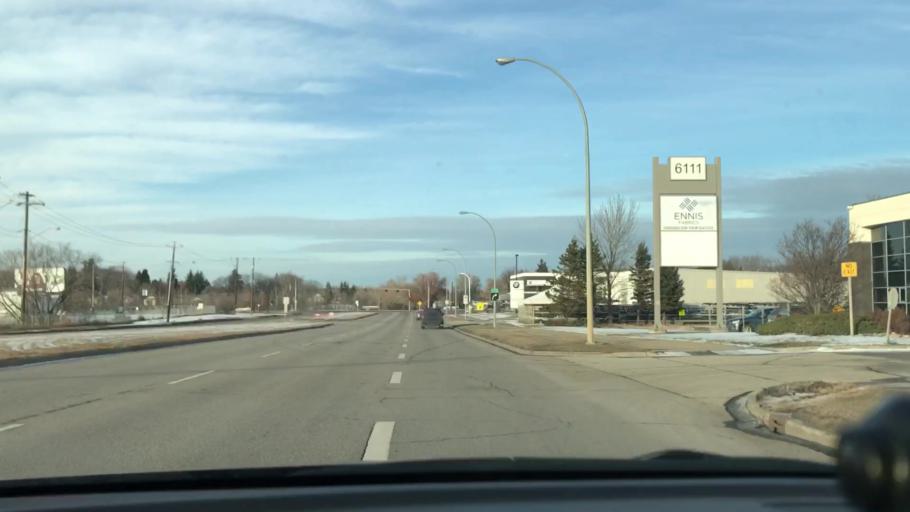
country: CA
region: Alberta
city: Edmonton
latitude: 53.4978
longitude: -113.4670
